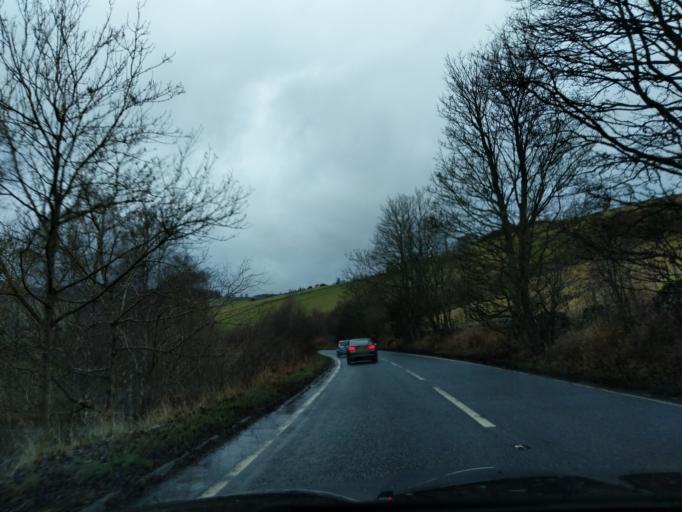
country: GB
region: Scotland
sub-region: The Scottish Borders
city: Galashiels
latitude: 55.6642
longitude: -2.8635
